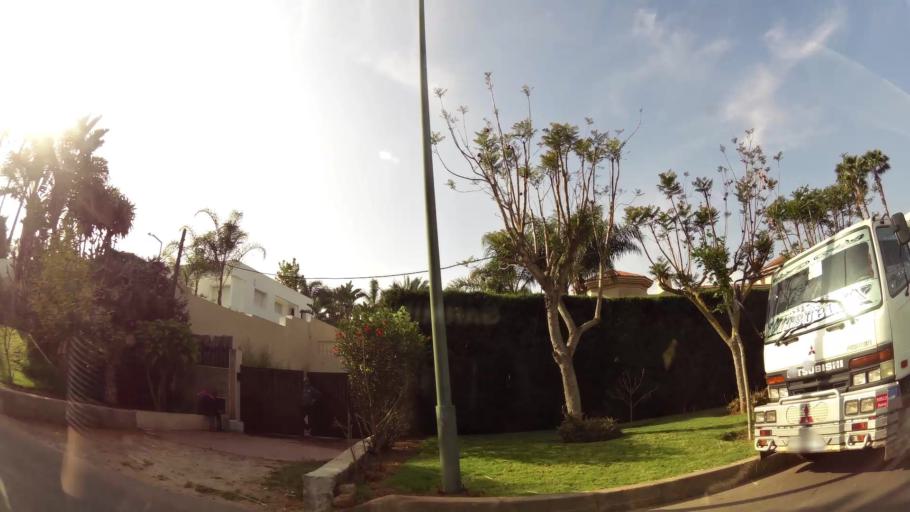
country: MA
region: Rabat-Sale-Zemmour-Zaer
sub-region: Rabat
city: Rabat
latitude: 33.9344
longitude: -6.8043
